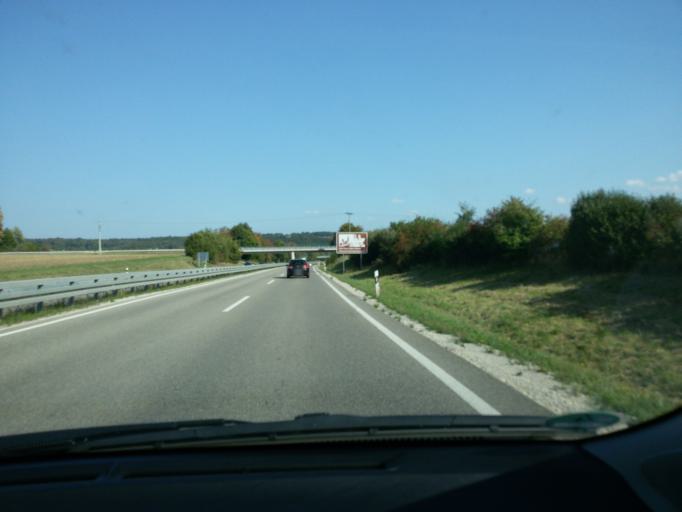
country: DE
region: Bavaria
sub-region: Swabia
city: Donauwoerth
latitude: 48.7396
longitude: 10.7598
